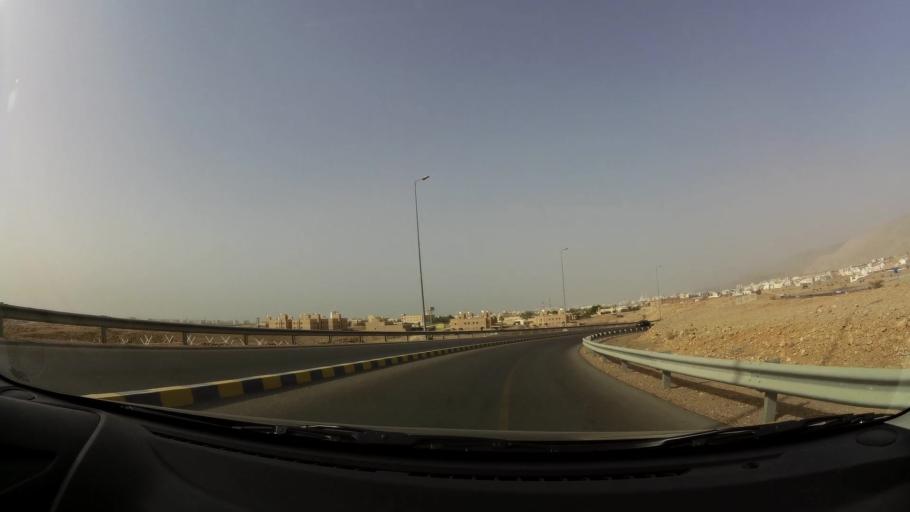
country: OM
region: Muhafazat Masqat
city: Bawshar
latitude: 23.5578
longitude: 58.3673
